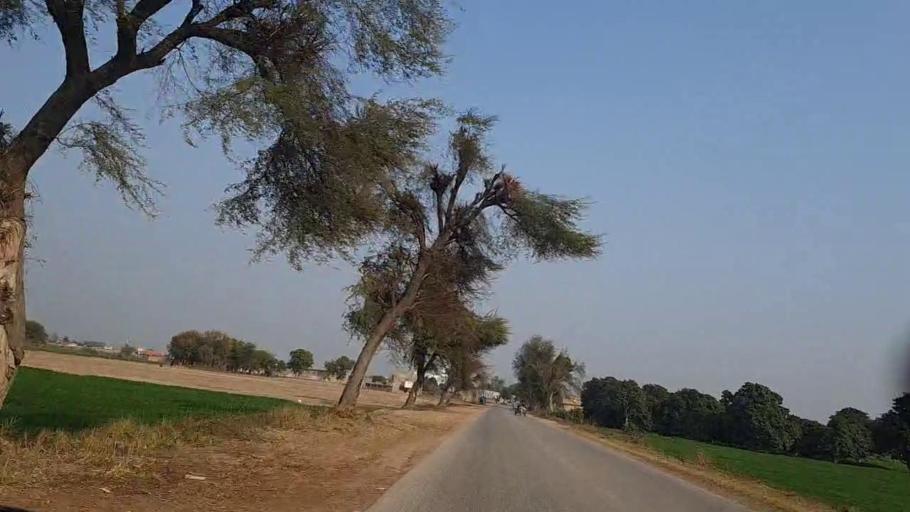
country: PK
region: Sindh
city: Sakrand
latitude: 26.1381
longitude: 68.2540
